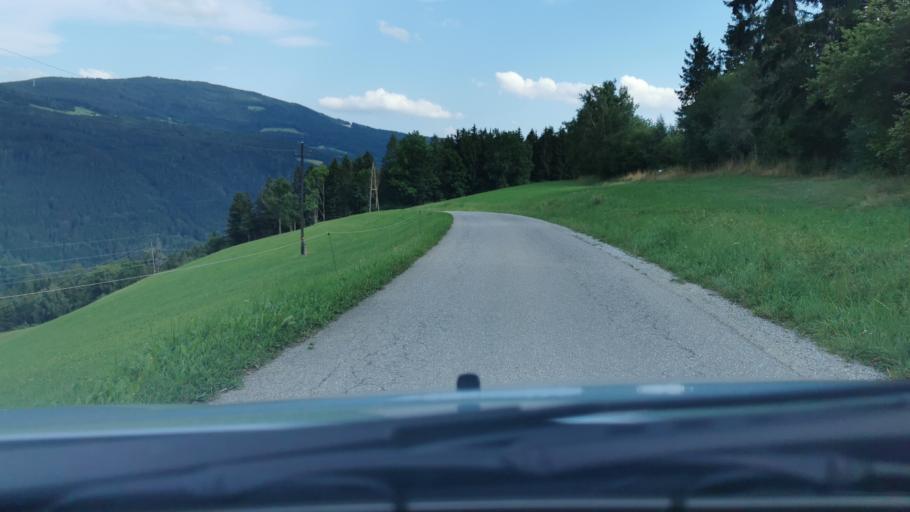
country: AT
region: Styria
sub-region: Politischer Bezirk Weiz
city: Koglhof
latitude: 47.3133
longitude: 15.6747
